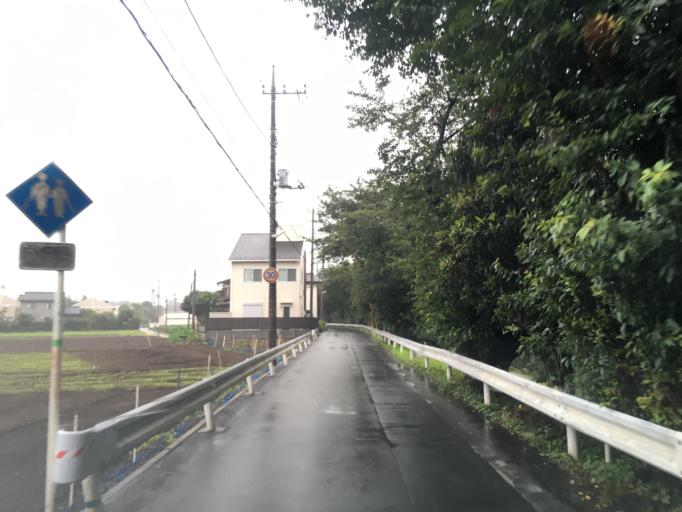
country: JP
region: Saitama
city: Tokorozawa
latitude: 35.7951
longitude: 139.4955
